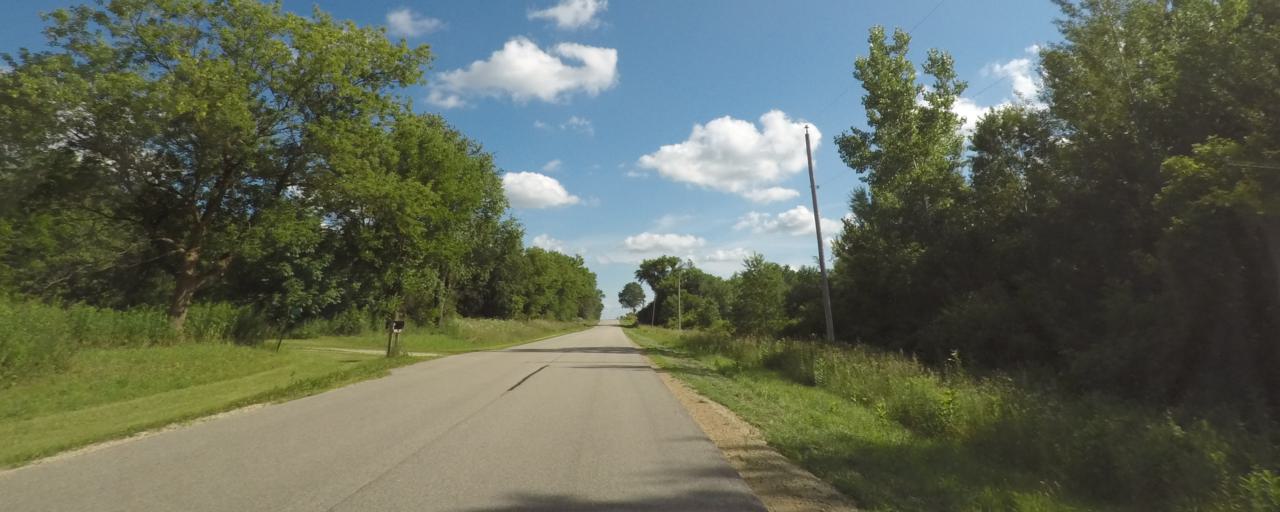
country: US
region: Wisconsin
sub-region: Dane County
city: Stoughton
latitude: 42.9033
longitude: -89.1320
